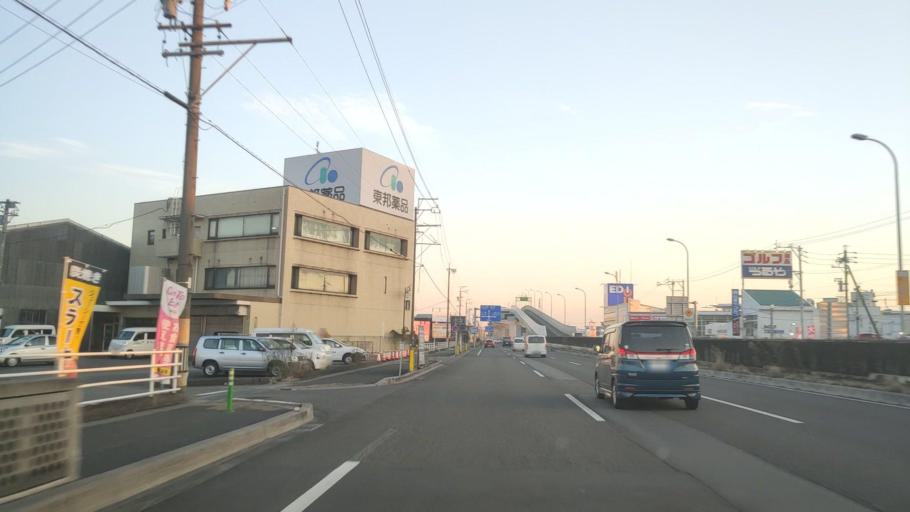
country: JP
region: Aichi
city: Ichinomiya
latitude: 35.2994
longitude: 136.8234
